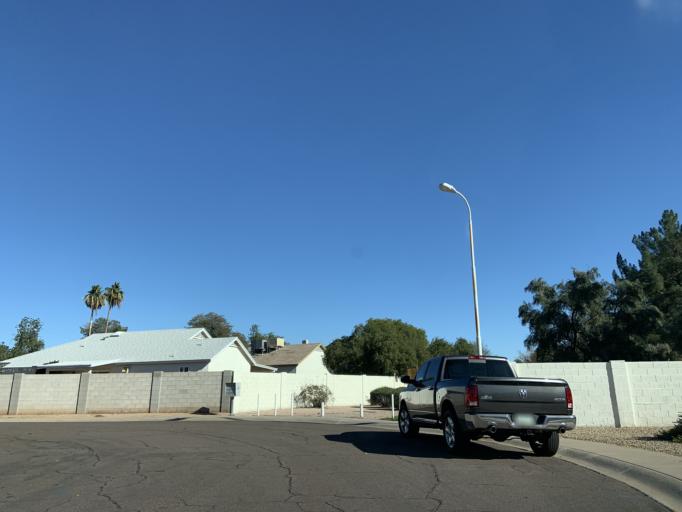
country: US
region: Arizona
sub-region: Maricopa County
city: San Carlos
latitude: 33.3543
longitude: -111.8707
